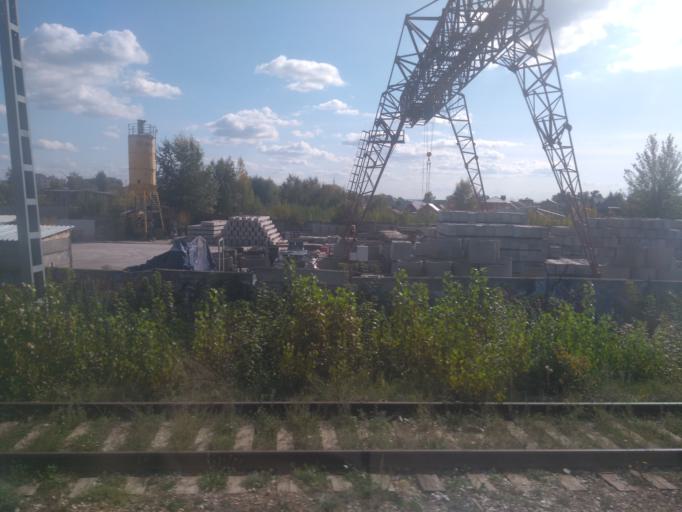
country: RU
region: Tatarstan
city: Verkhniy Uslon
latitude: 55.8038
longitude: 49.0361
